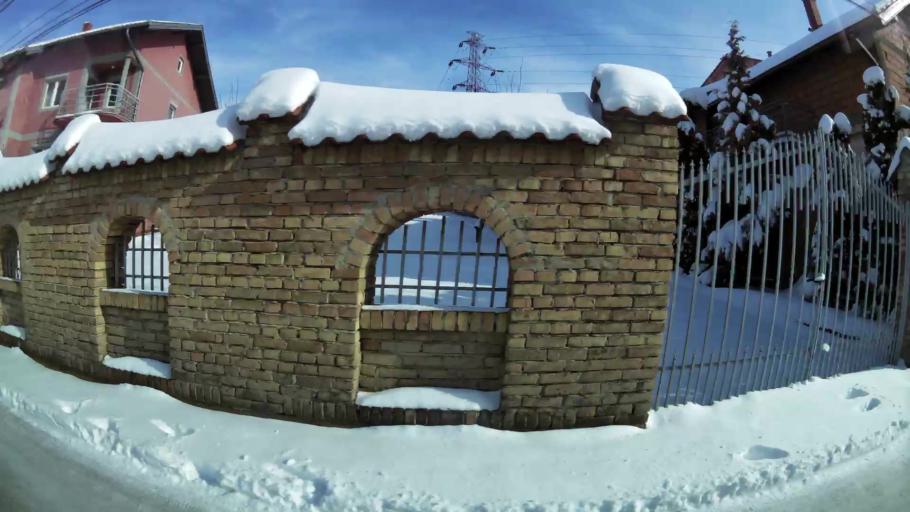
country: RS
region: Central Serbia
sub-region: Belgrade
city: Palilula
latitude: 44.7992
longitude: 20.5282
